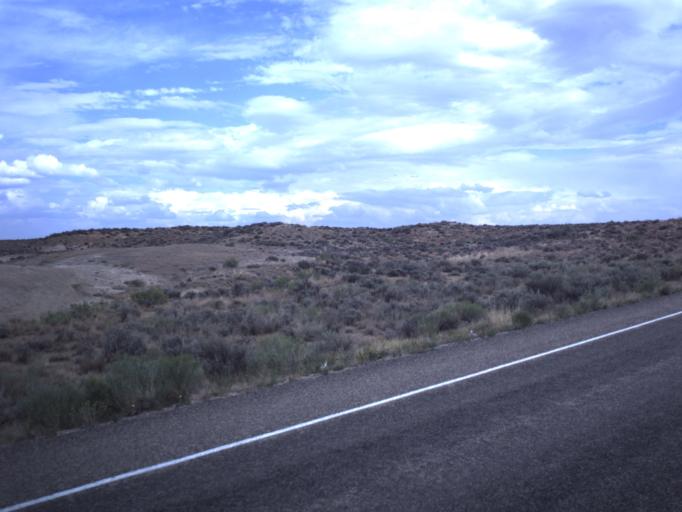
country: US
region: Colorado
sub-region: Rio Blanco County
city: Rangely
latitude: 40.0856
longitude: -109.2177
